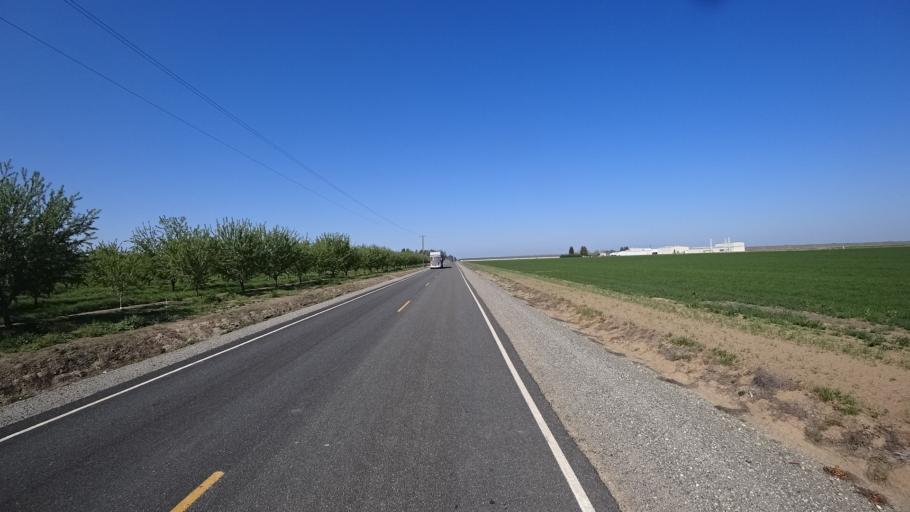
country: US
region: California
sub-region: Glenn County
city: Hamilton City
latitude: 39.6597
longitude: -122.0478
